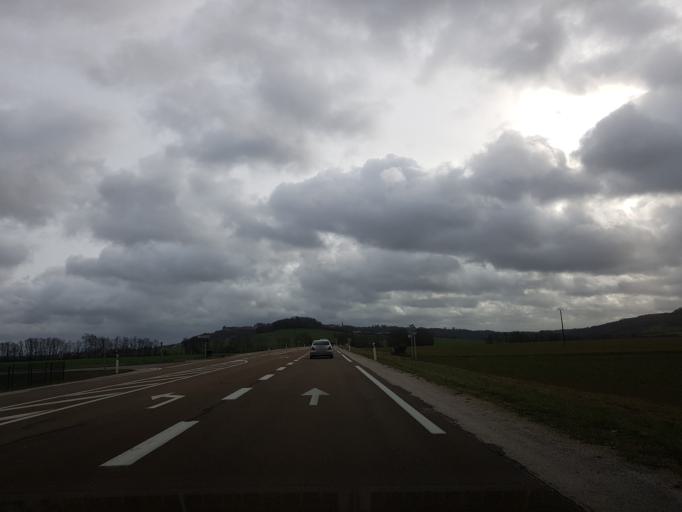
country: FR
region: Champagne-Ardenne
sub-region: Departement de la Haute-Marne
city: Langres
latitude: 47.8884
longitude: 5.3167
